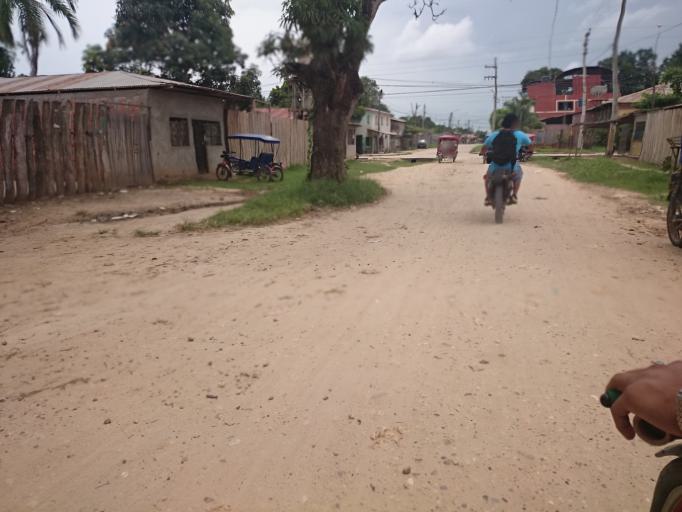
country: PE
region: Ucayali
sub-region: Provincia de Coronel Portillo
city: Pucallpa
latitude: -8.3756
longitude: -74.5566
